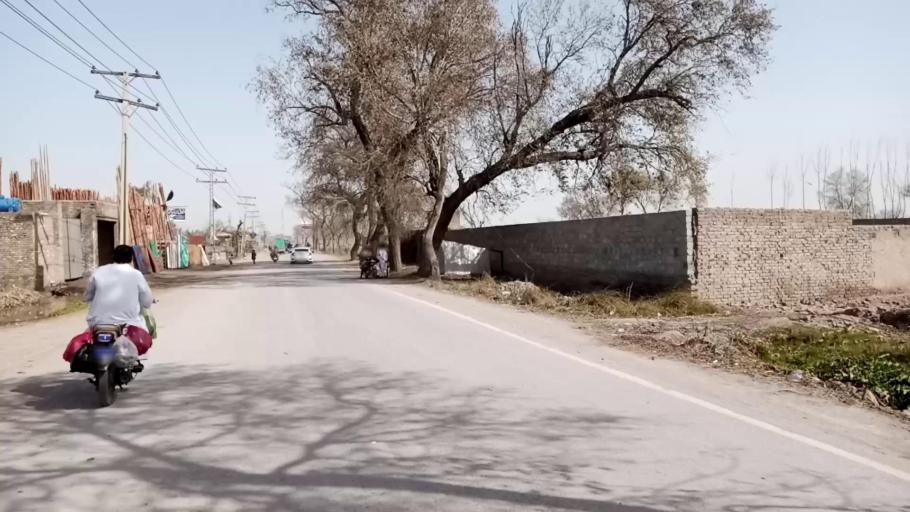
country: PK
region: Khyber Pakhtunkhwa
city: Peshawar
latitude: 33.9976
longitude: 71.6344
